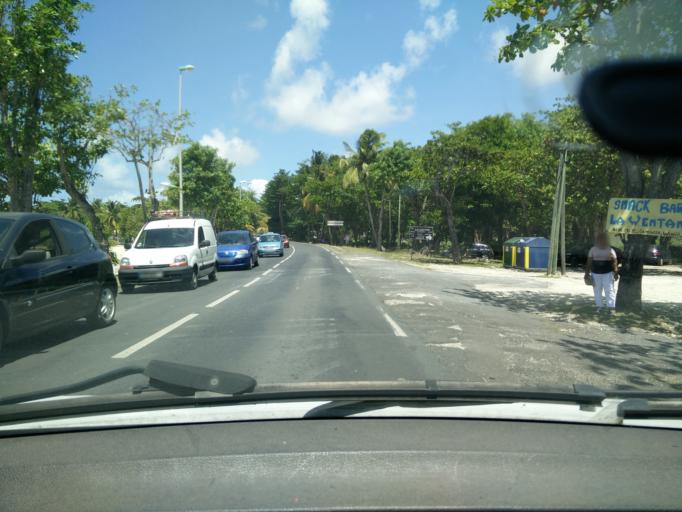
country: GP
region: Guadeloupe
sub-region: Guadeloupe
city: Le Moule
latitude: 16.3349
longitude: -61.3686
